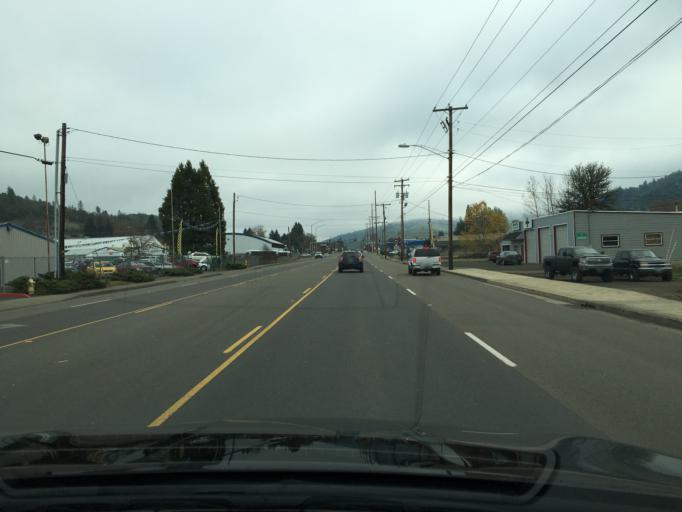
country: US
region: Oregon
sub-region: Douglas County
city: Roseburg
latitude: 43.2130
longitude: -123.3253
